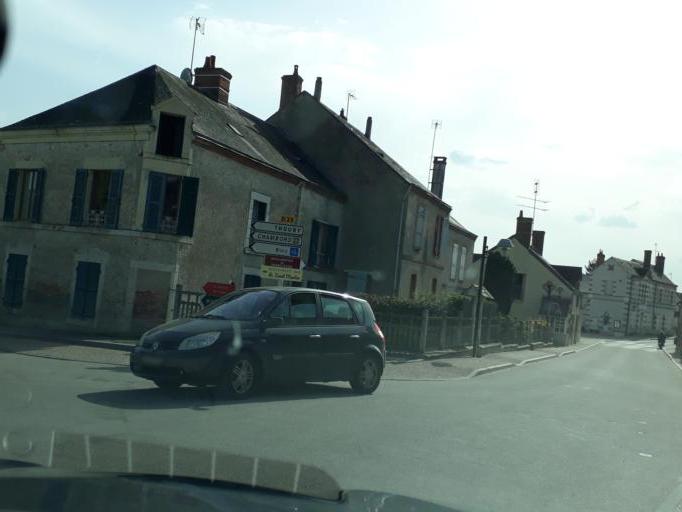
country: FR
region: Centre
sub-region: Departement du Loir-et-Cher
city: Saint-Laurent-Nouan
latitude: 47.6507
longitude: 1.6091
